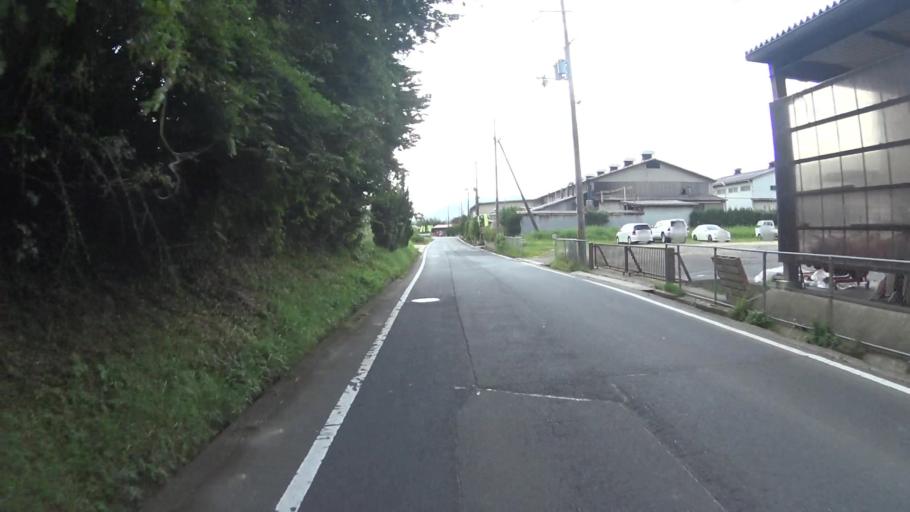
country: JP
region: Kyoto
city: Miyazu
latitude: 35.6345
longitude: 135.0831
